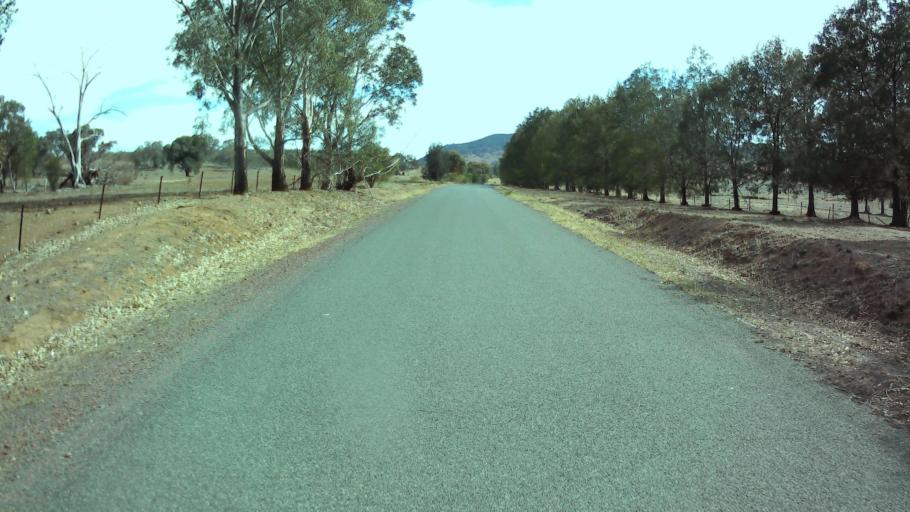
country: AU
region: New South Wales
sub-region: Weddin
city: Grenfell
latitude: -33.8112
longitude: 148.2927
